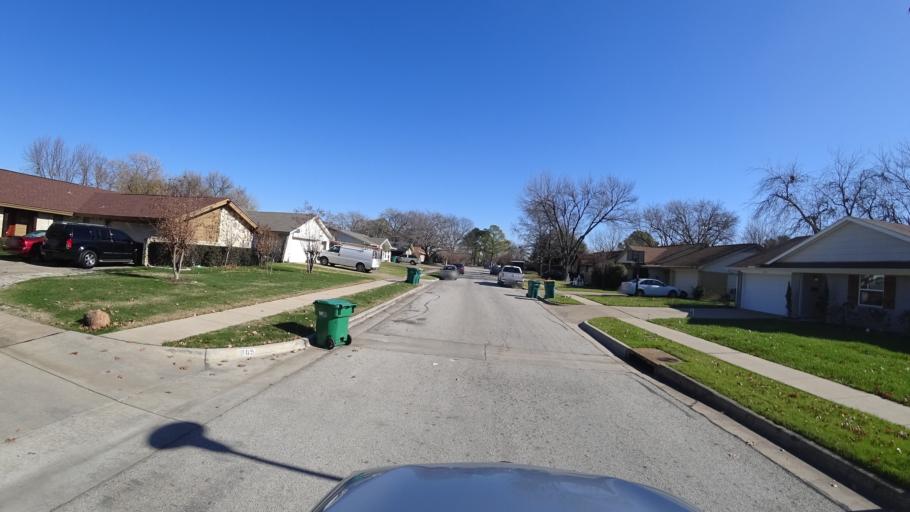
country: US
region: Texas
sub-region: Denton County
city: Lewisville
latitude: 33.0330
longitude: -97.0180
